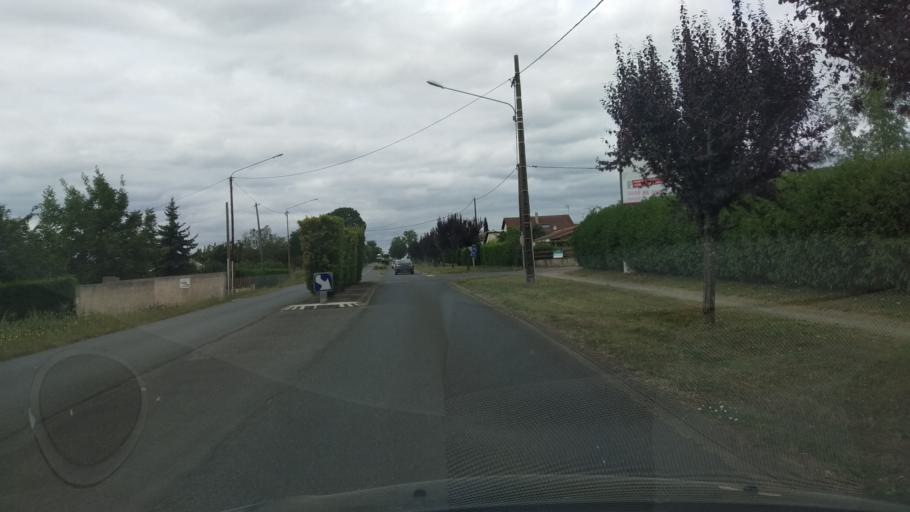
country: FR
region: Poitou-Charentes
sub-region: Departement de la Vienne
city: Roches-Premarie-Andille
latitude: 46.4877
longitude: 0.3689
